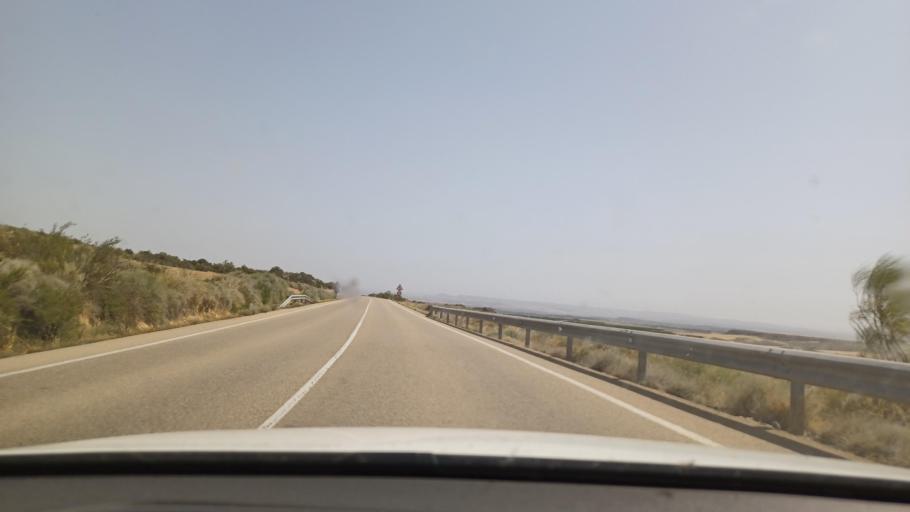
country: ES
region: Aragon
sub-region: Provincia de Zaragoza
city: Chiprana
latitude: 41.3326
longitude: -0.0893
